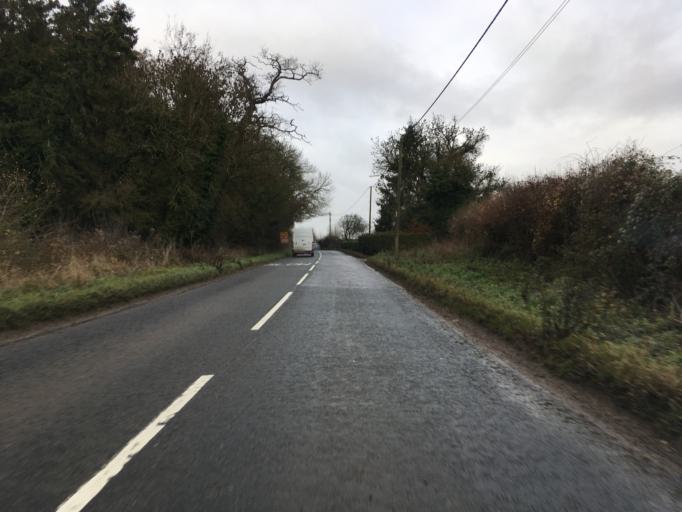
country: GB
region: England
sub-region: Wiltshire
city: Malmesbury
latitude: 51.6110
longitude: -2.1173
